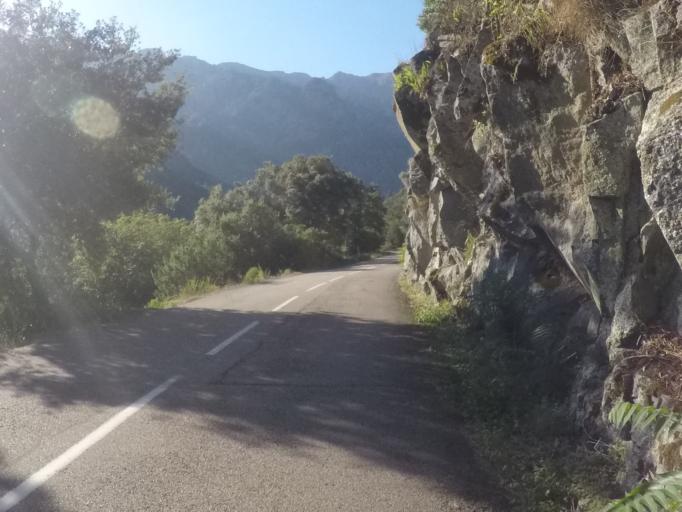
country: FR
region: Corsica
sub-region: Departement de la Corse-du-Sud
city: Cargese
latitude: 42.2467
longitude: 8.7302
